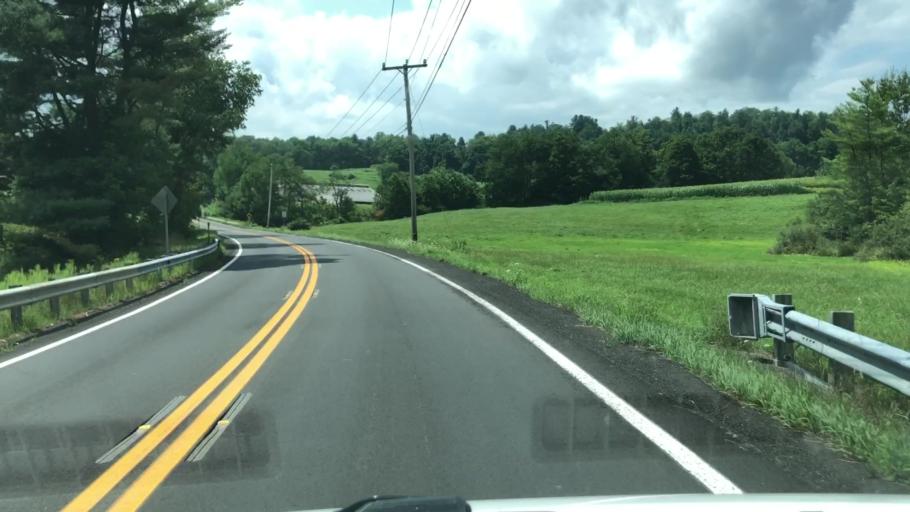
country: US
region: Massachusetts
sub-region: Franklin County
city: Ashfield
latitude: 42.5181
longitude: -72.7525
